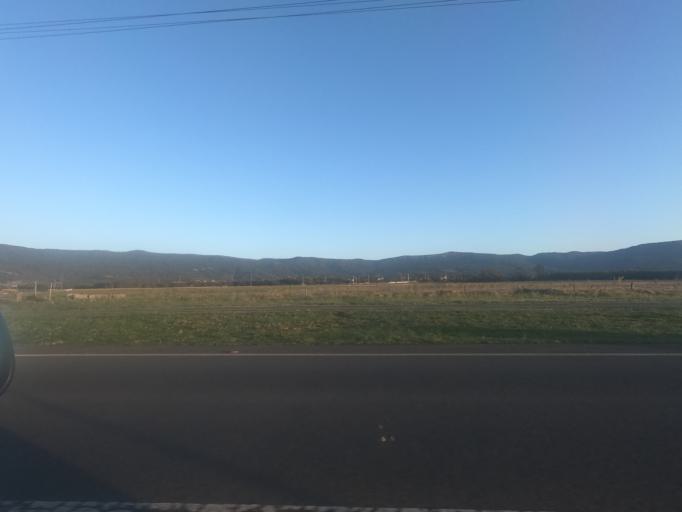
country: AU
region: New South Wales
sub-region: Wollongong
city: Dapto
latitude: -34.5026
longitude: 150.7819
